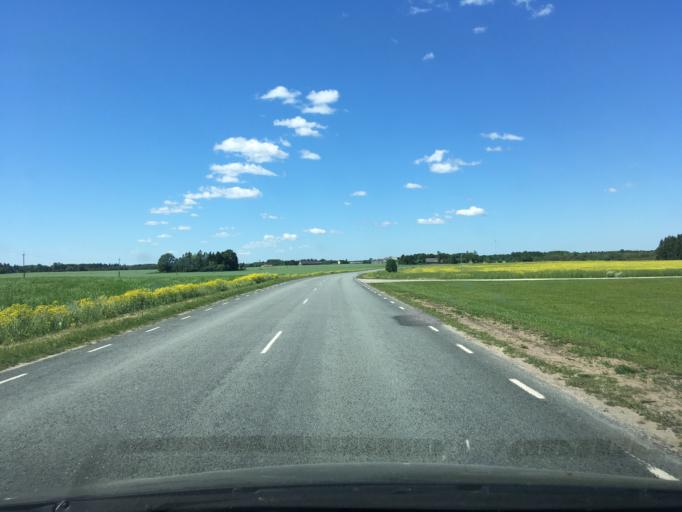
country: EE
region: Harju
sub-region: Rae vald
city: Vaida
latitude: 59.1858
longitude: 25.0174
